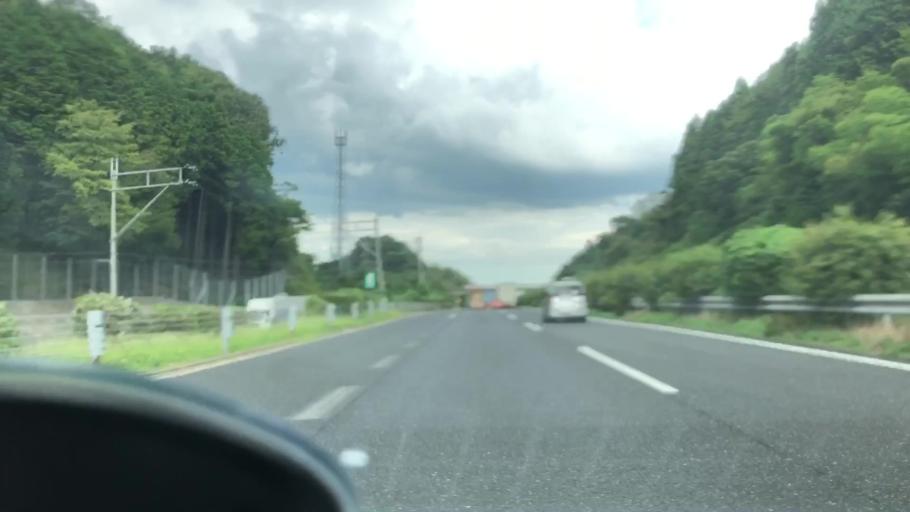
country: JP
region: Hyogo
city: Yamazakicho-nakabirose
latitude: 34.9756
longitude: 134.6435
